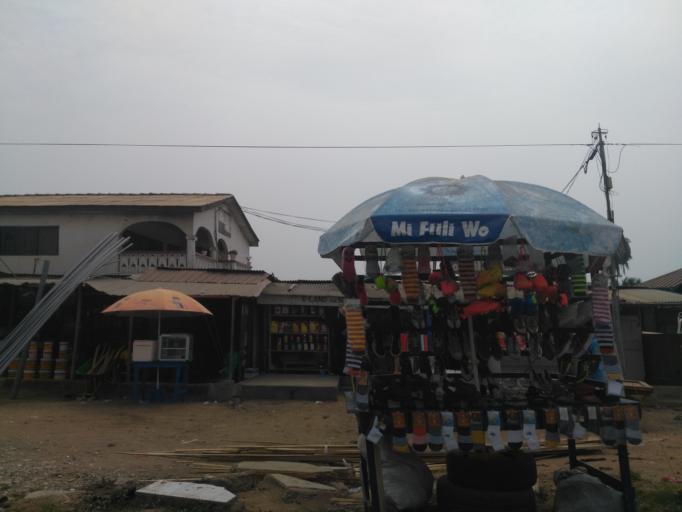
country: GH
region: Greater Accra
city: Nungua
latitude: 5.5982
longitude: -0.0819
